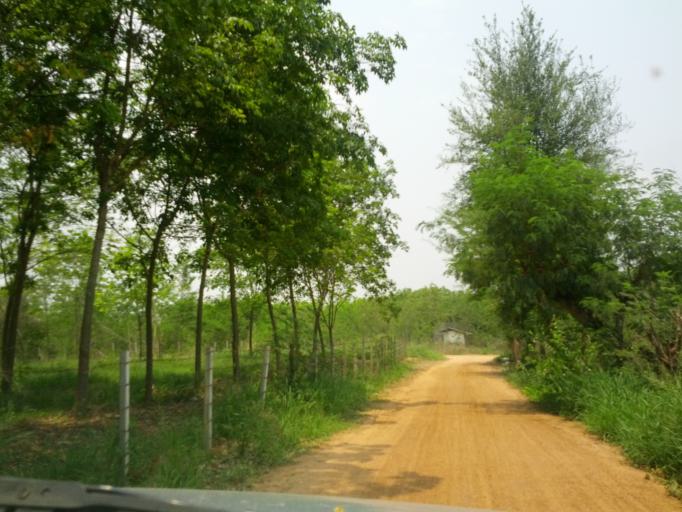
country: TH
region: Chiang Mai
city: San Sai
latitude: 18.9171
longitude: 99.0380
